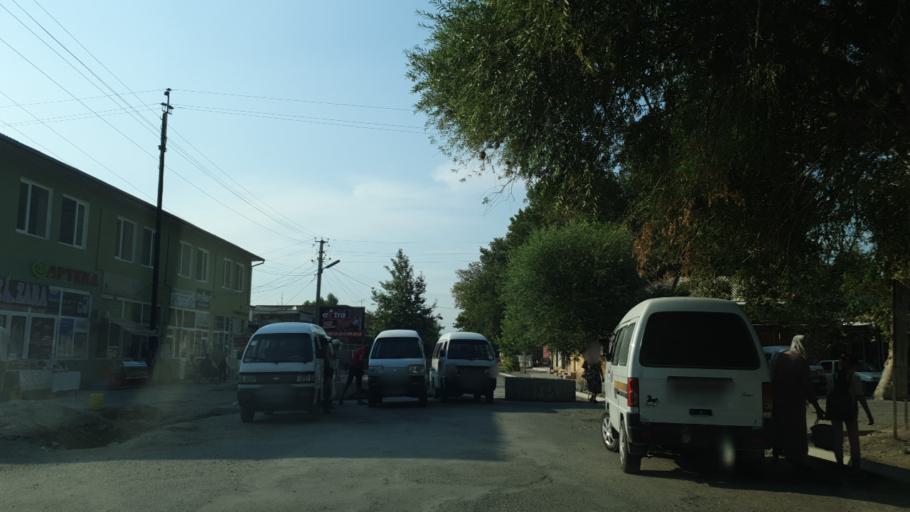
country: UZ
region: Fergana
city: Yaypan
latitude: 40.3787
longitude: 70.8110
